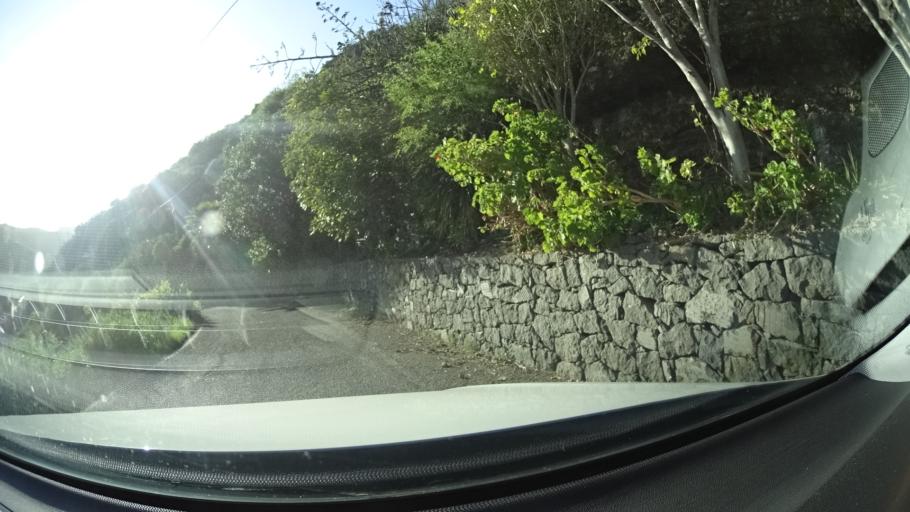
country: ES
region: Canary Islands
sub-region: Provincia de Las Palmas
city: Artenara
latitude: 28.0461
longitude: -15.6575
